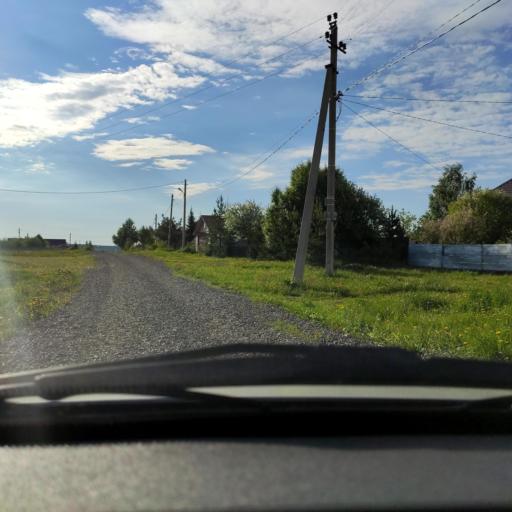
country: RU
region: Bashkortostan
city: Iglino
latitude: 54.7911
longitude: 56.3167
